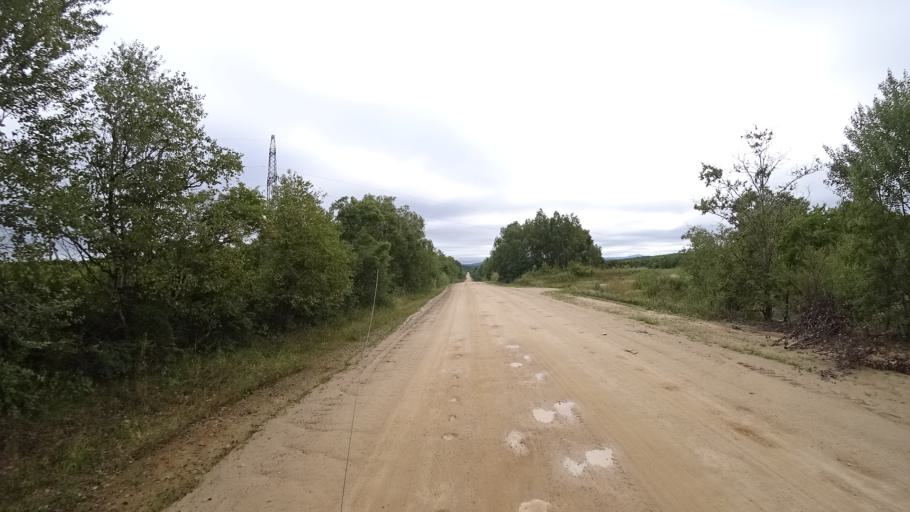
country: RU
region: Primorskiy
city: Monastyrishche
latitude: 44.1100
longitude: 132.6189
